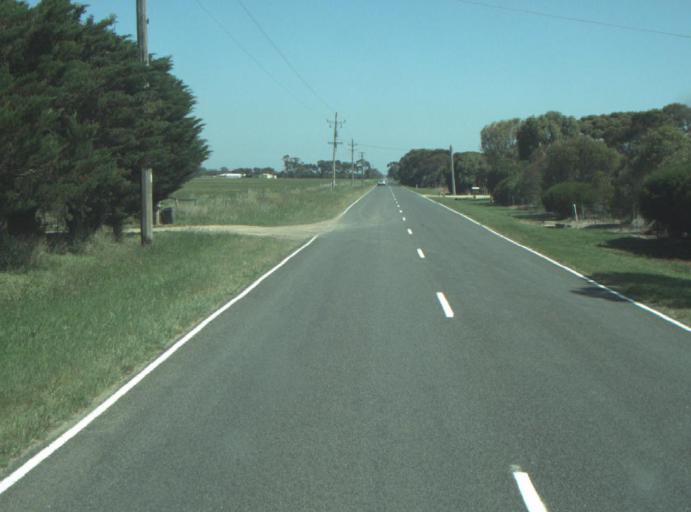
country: AU
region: Victoria
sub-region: Greater Geelong
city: Lara
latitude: -37.9854
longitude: 144.4031
